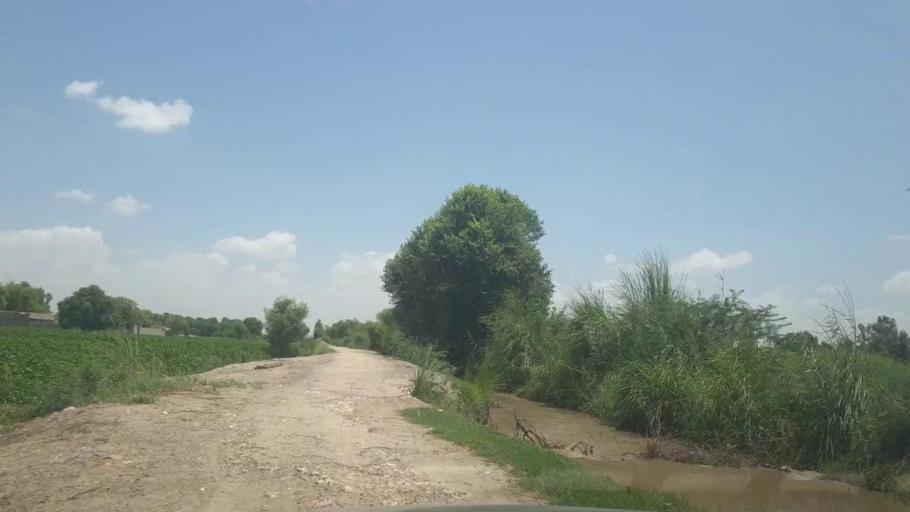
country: PK
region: Sindh
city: Kot Diji
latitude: 27.2633
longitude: 69.0226
